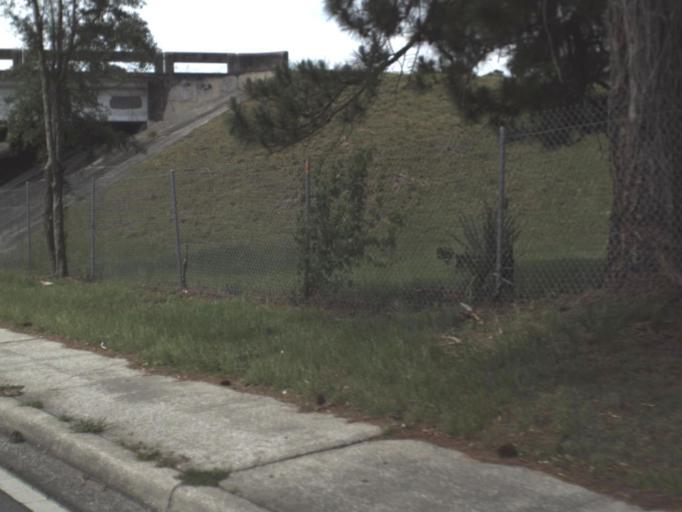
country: US
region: Florida
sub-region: Duval County
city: Jacksonville
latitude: 30.2975
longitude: -81.6017
